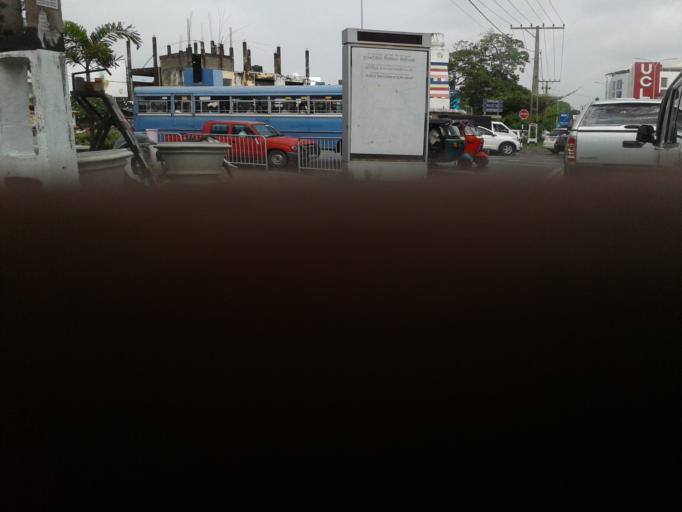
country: LK
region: Western
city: Battaramulla South
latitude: 6.9048
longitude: 79.9058
